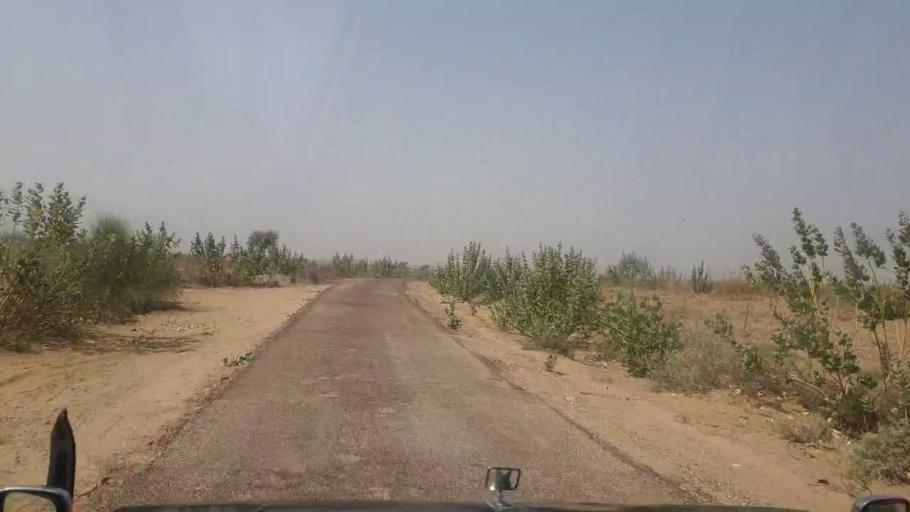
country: PK
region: Sindh
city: Islamkot
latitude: 25.0953
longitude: 70.1755
